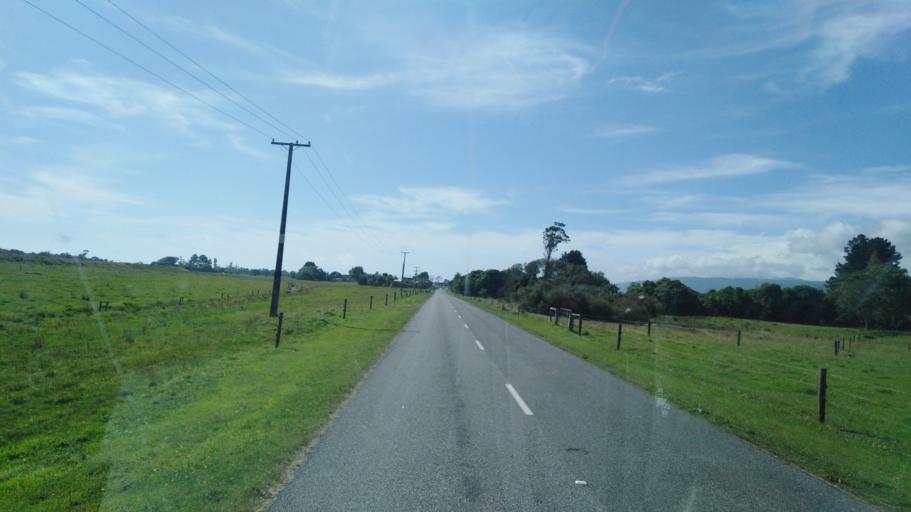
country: NZ
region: West Coast
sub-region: Buller District
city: Westport
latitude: -41.2564
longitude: 172.1309
